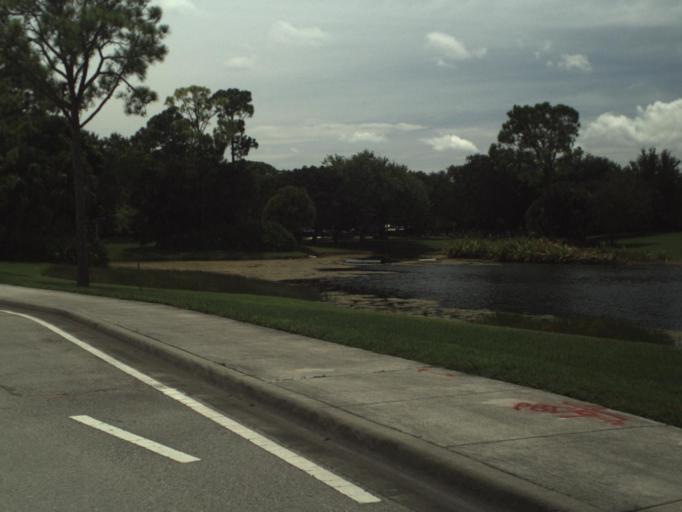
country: US
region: Florida
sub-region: Palm Beach County
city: Palm Beach Gardens
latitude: 26.8392
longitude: -80.1373
